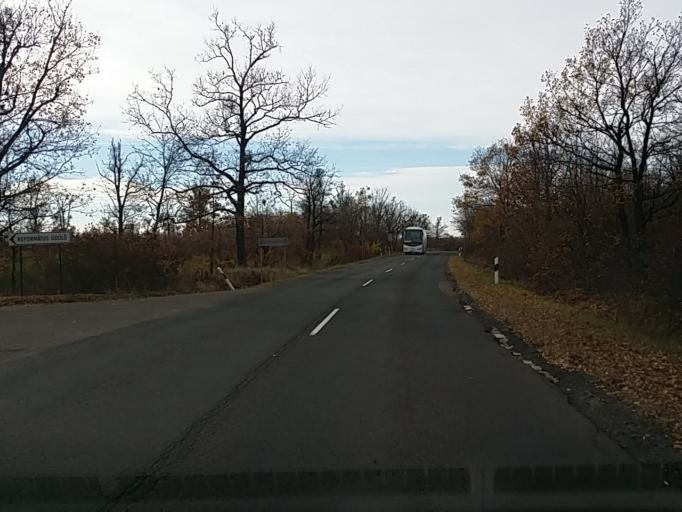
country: HU
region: Heves
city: Gyongyossolymos
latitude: 47.8529
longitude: 19.9702
